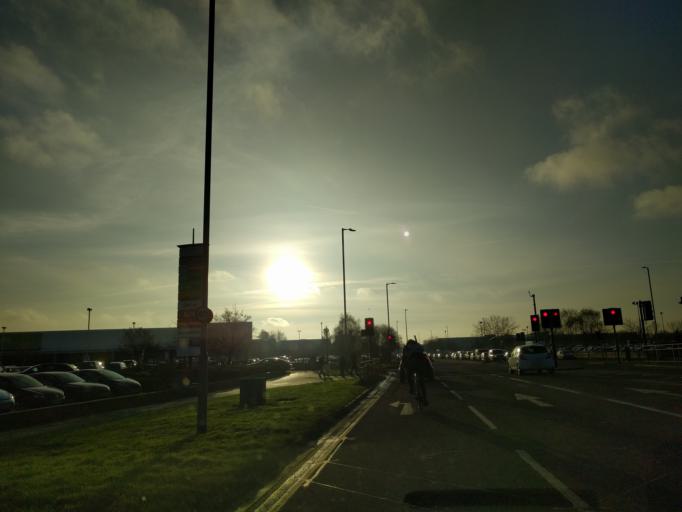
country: GB
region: England
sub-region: Lincolnshire
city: Lincoln
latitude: 53.2246
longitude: -0.5523
